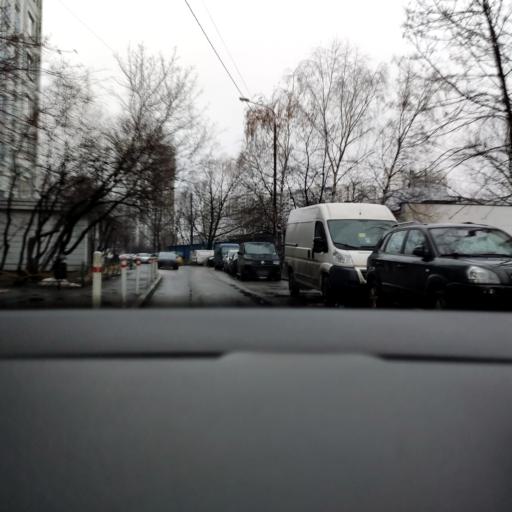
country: RU
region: Moskovskaya
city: Reutov
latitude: 55.7416
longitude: 37.8688
